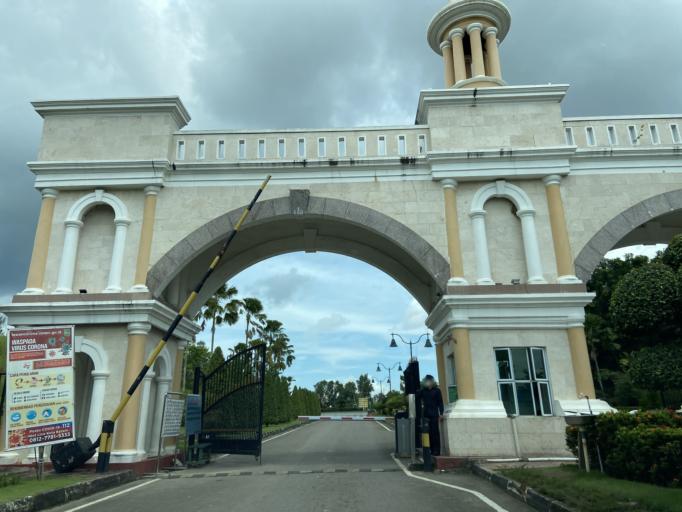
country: SG
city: Singapore
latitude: 1.1306
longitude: 103.9997
